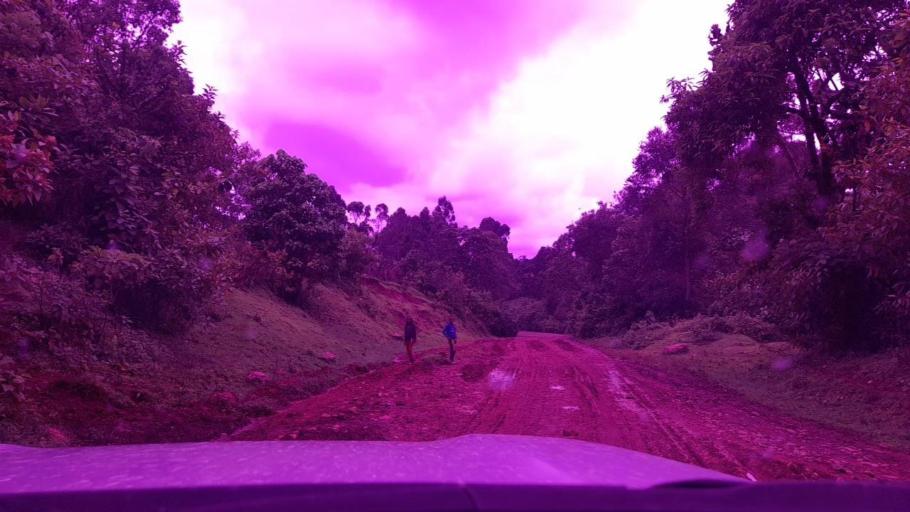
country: ET
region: Southern Nations, Nationalities, and People's Region
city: Tippi
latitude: 7.5693
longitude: 35.7843
